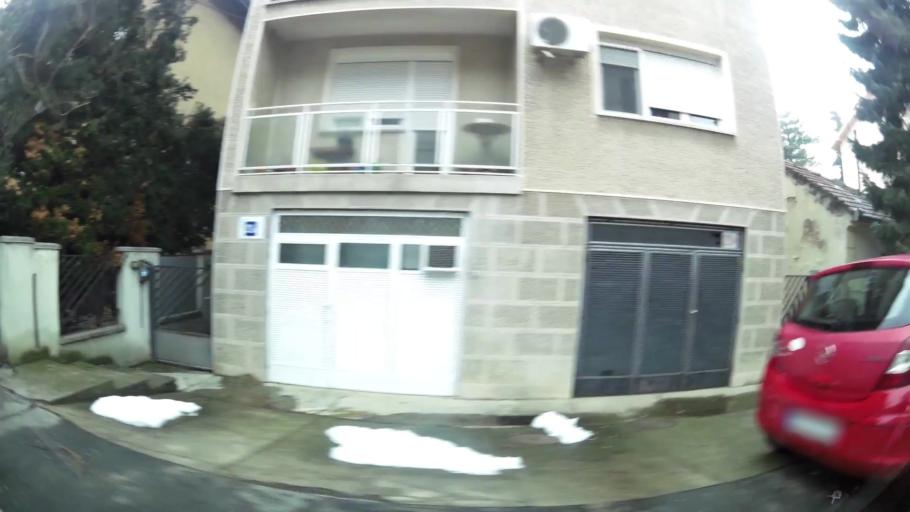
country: RS
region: Central Serbia
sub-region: Belgrade
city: Vozdovac
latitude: 44.7769
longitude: 20.4793
